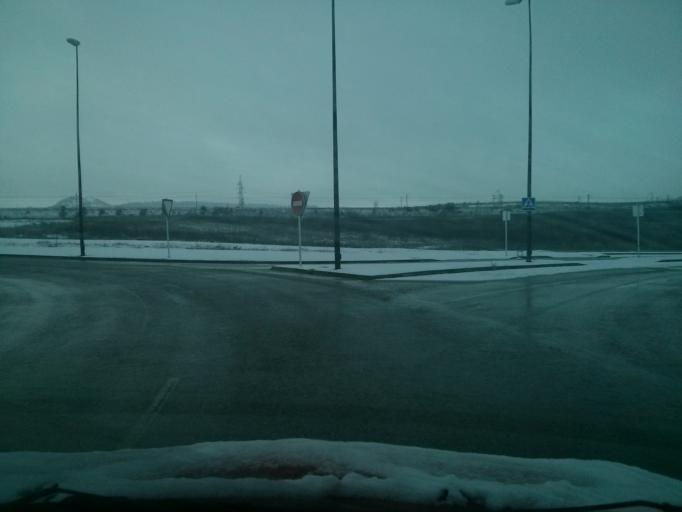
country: ES
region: Castille and Leon
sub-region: Provincia de Burgos
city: Burgos
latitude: 42.3709
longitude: -3.6982
